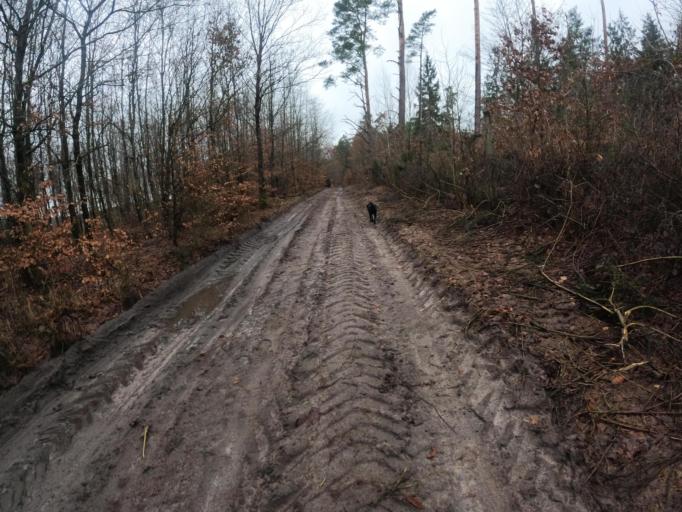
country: PL
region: West Pomeranian Voivodeship
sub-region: Powiat slawienski
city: Slawno
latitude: 54.2415
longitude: 16.6923
